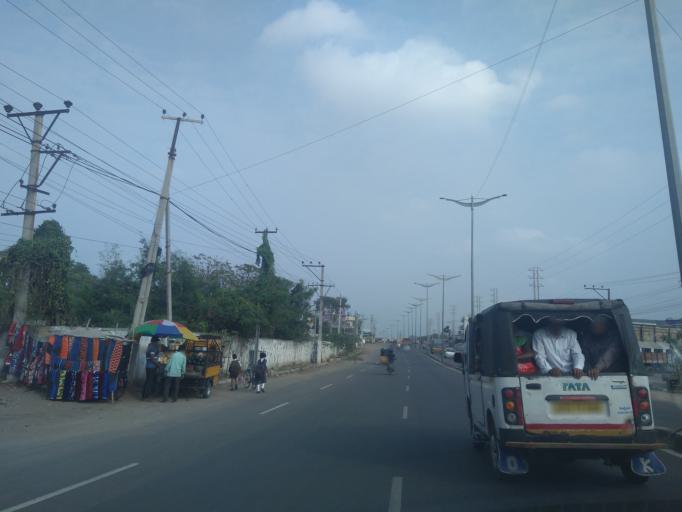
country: IN
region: Telangana
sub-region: Rangareddi
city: Balapur
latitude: 17.3164
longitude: 78.4536
